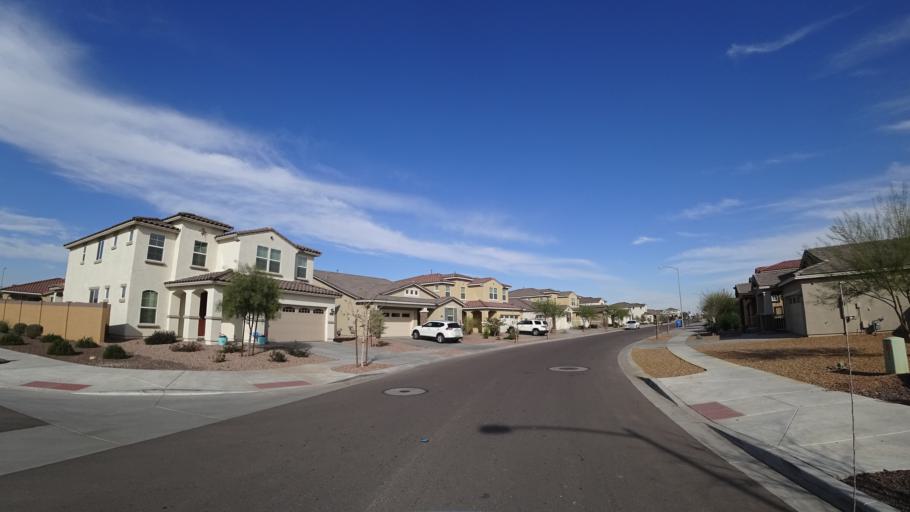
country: US
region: Arizona
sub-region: Maricopa County
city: Tolleson
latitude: 33.4316
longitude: -112.2845
